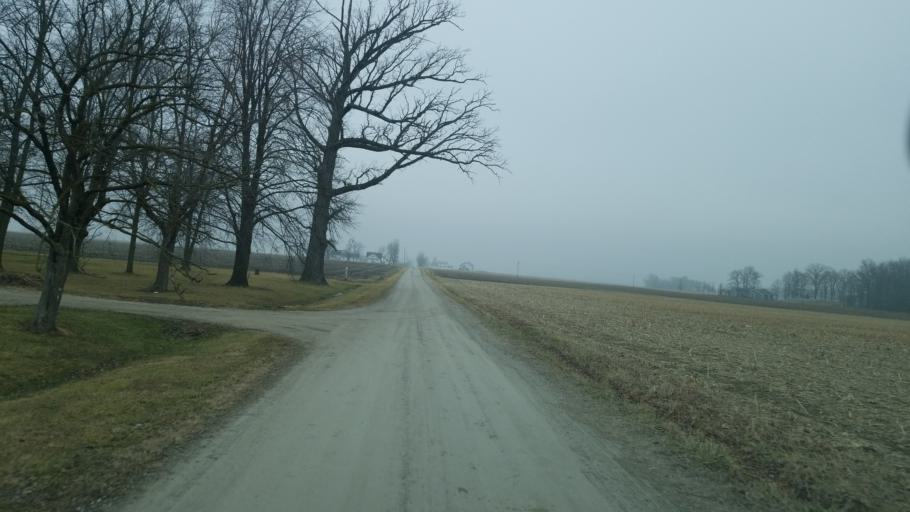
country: US
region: Indiana
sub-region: Adams County
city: Berne
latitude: 40.6957
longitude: -85.0135
